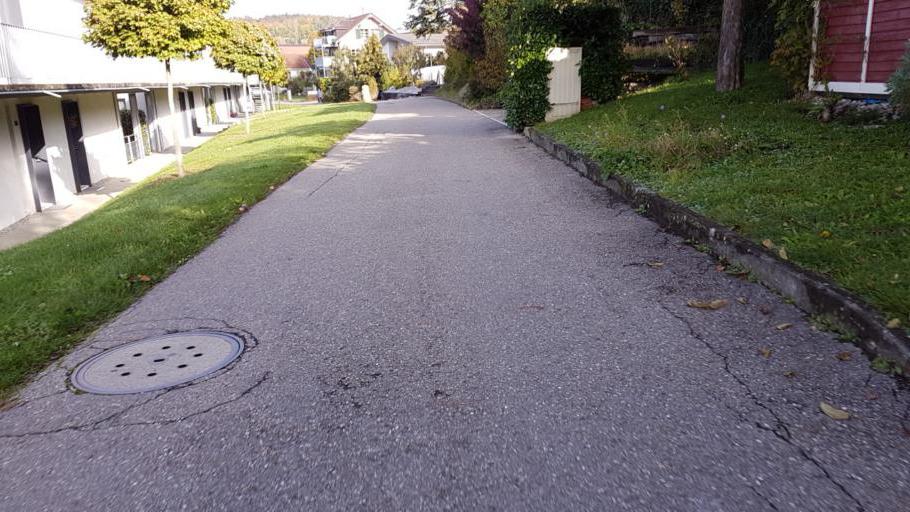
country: CH
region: Bern
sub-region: Bern-Mittelland District
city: Worb
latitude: 46.9253
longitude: 7.5456
